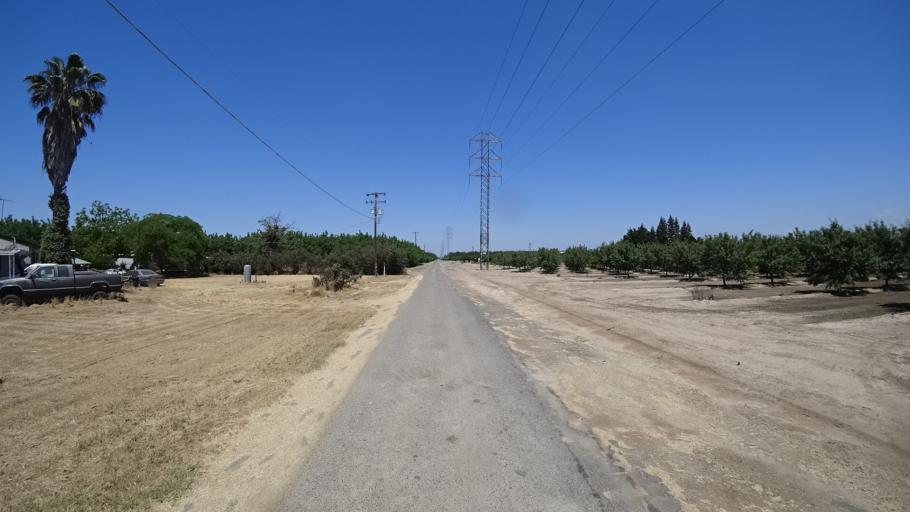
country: US
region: California
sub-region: Fresno County
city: Kingsburg
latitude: 36.4416
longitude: -119.5916
